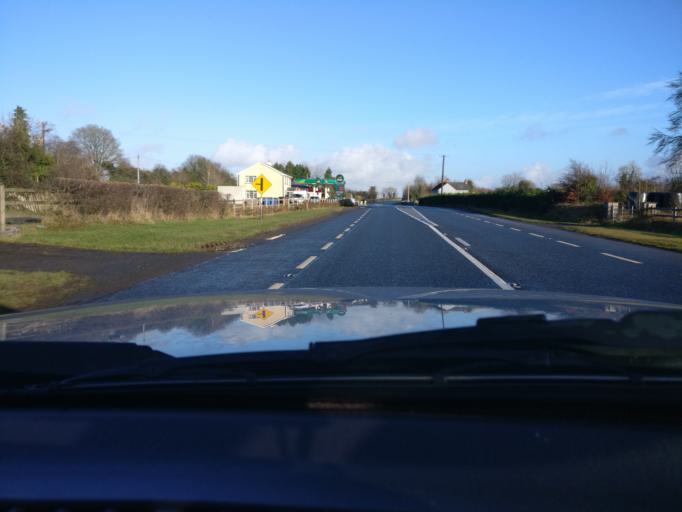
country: IE
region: Leinster
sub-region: An Iarmhi
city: An Muileann gCearr
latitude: 53.5503
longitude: -7.2766
